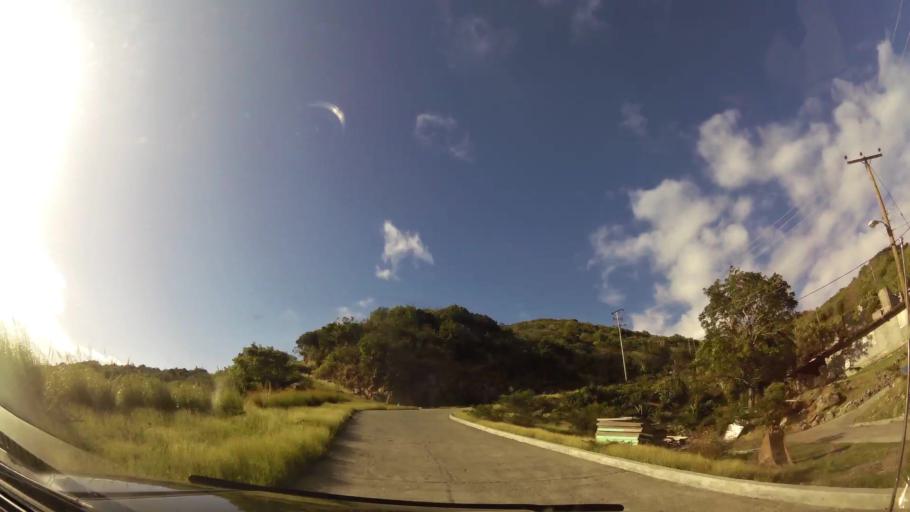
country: MS
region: Saint Peter
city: Brades
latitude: 16.8016
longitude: -62.1945
